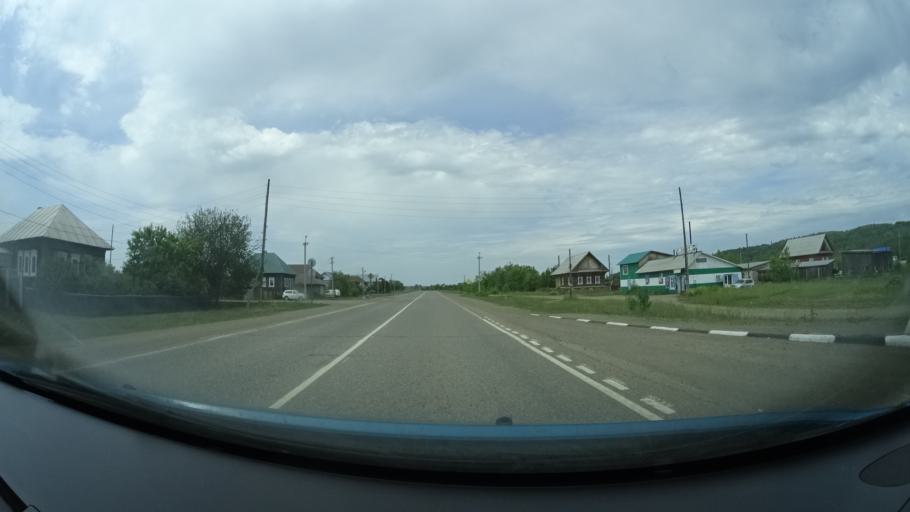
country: RU
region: Perm
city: Barda
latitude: 56.8276
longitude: 55.6265
